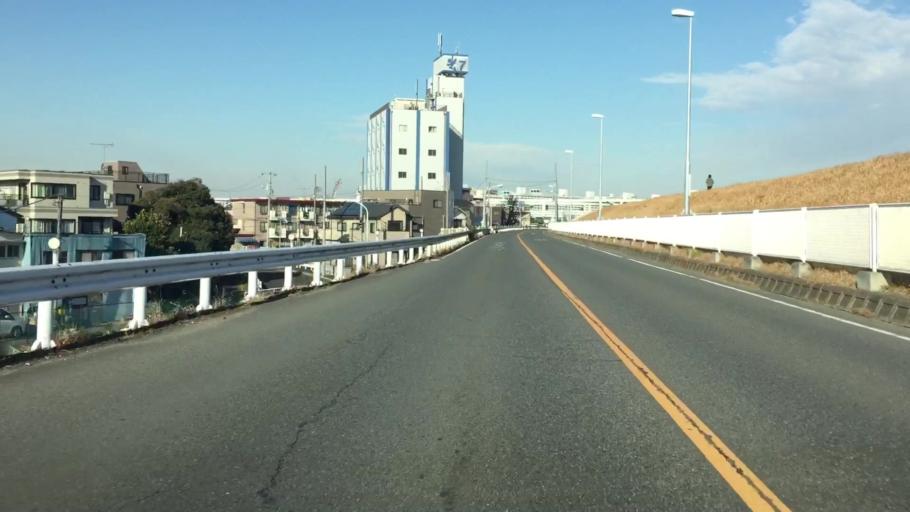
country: JP
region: Saitama
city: Kawaguchi
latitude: 35.7581
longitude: 139.7631
